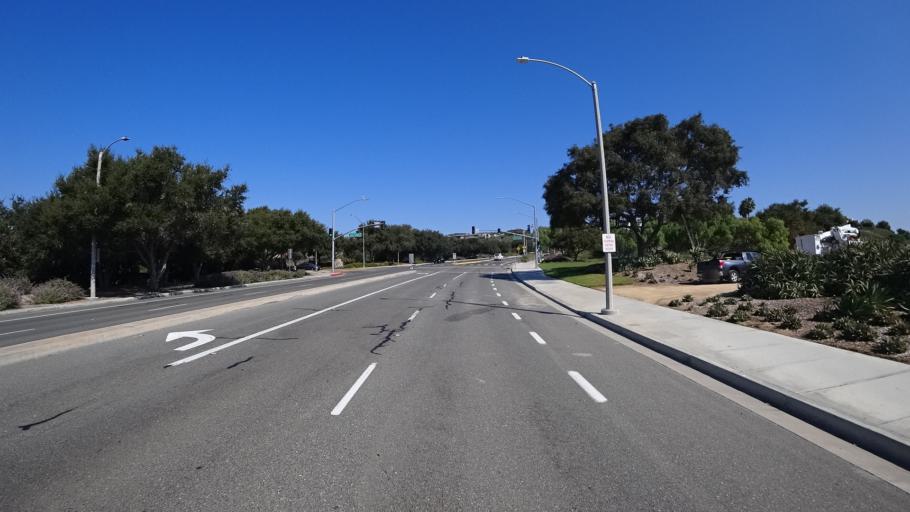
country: US
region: California
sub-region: Orange County
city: San Clemente
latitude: 33.4721
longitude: -117.5975
